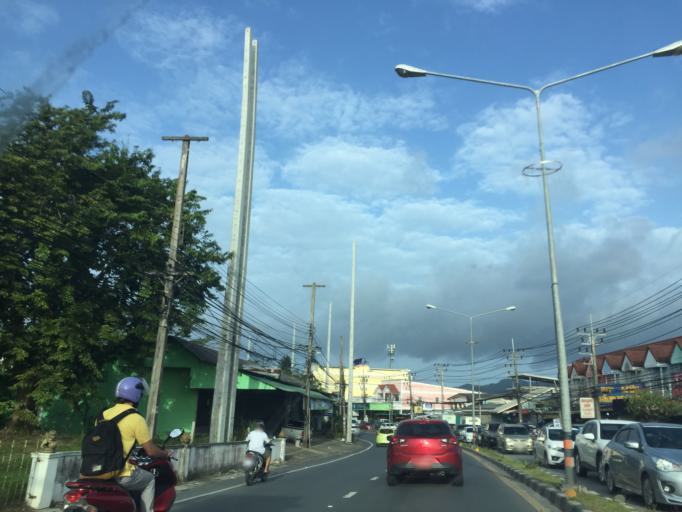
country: TH
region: Phuket
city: Mueang Phuket
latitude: 7.8669
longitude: 98.3730
